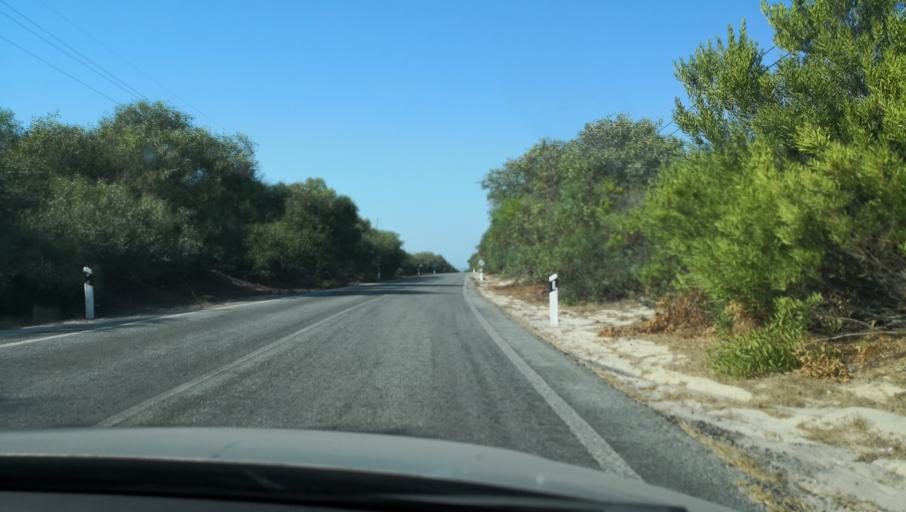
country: PT
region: Setubal
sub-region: Setubal
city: Setubal
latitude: 38.4127
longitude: -8.8145
